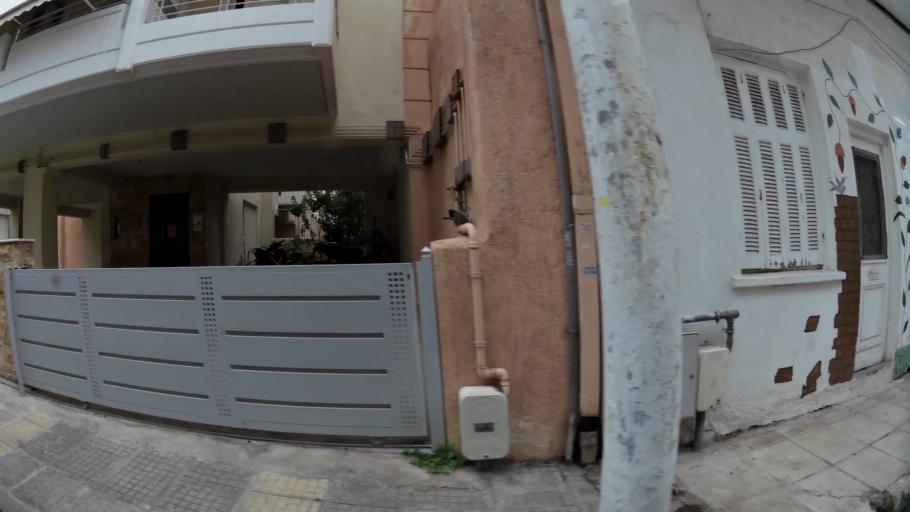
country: GR
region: Attica
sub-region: Nomarchia Athinas
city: Aigaleo
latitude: 38.0007
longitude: 23.6822
